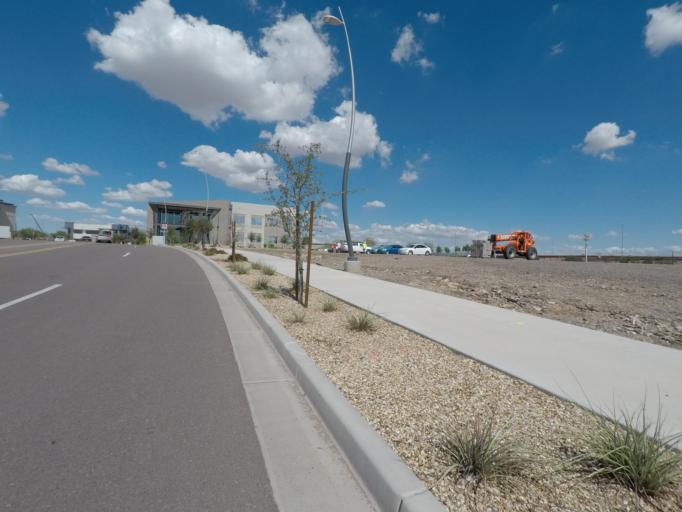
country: US
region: Arizona
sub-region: Maricopa County
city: Tempe
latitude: 33.4302
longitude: -111.8970
